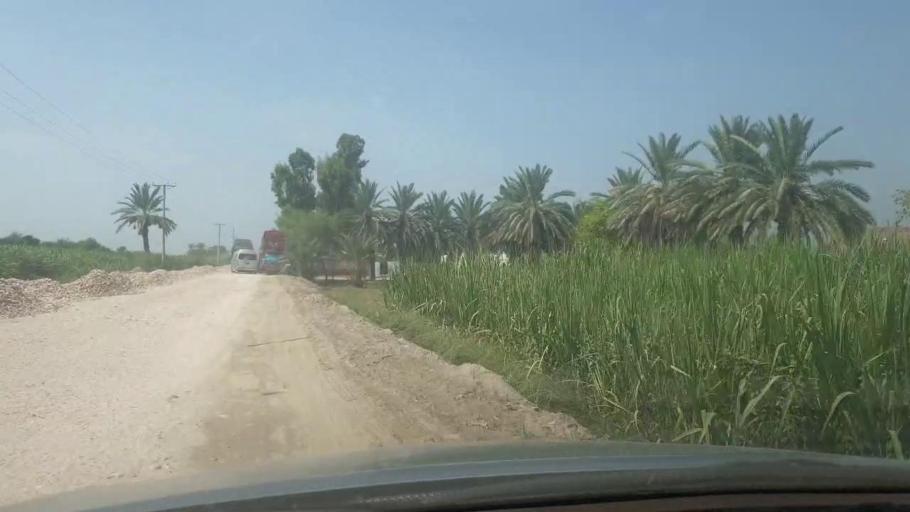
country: PK
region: Sindh
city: Ranipur
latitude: 27.2781
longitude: 68.5991
